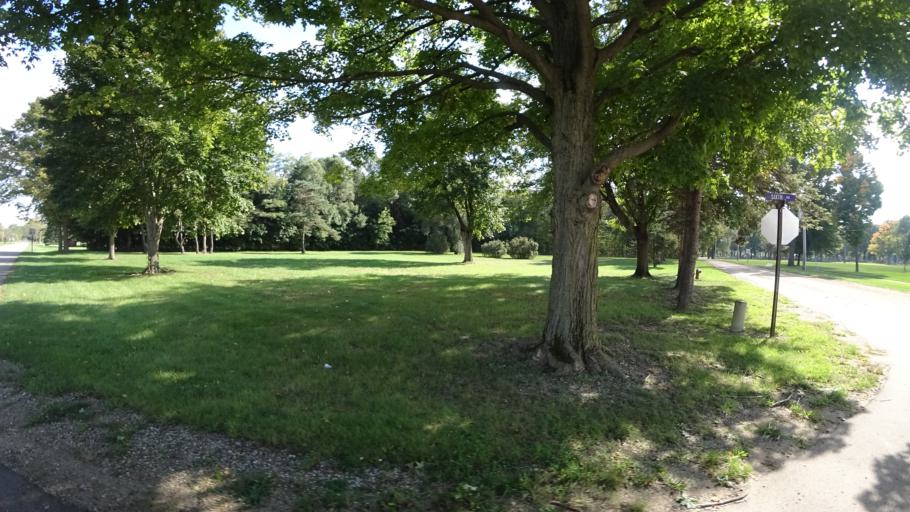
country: US
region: Michigan
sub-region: Saint Joseph County
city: Three Rivers
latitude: 41.9474
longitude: -85.6151
